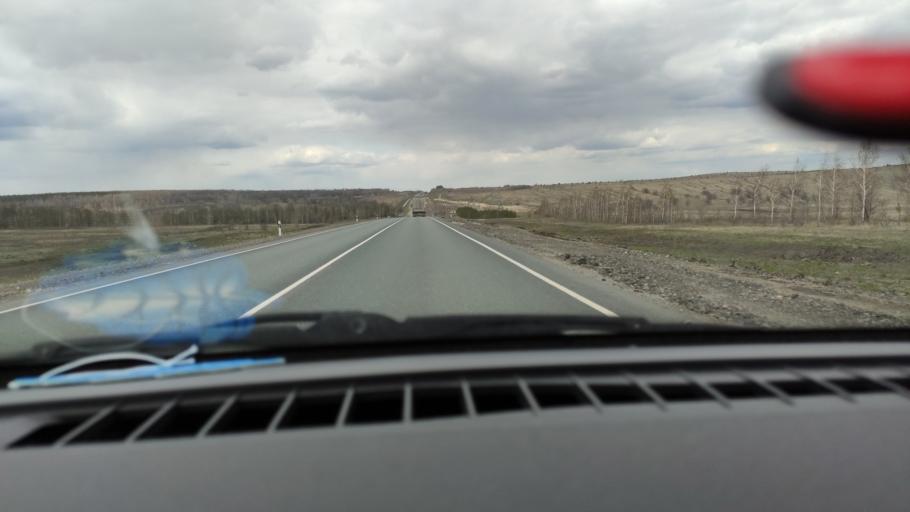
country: RU
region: Saratov
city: Shikhany
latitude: 52.1362
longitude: 47.2178
